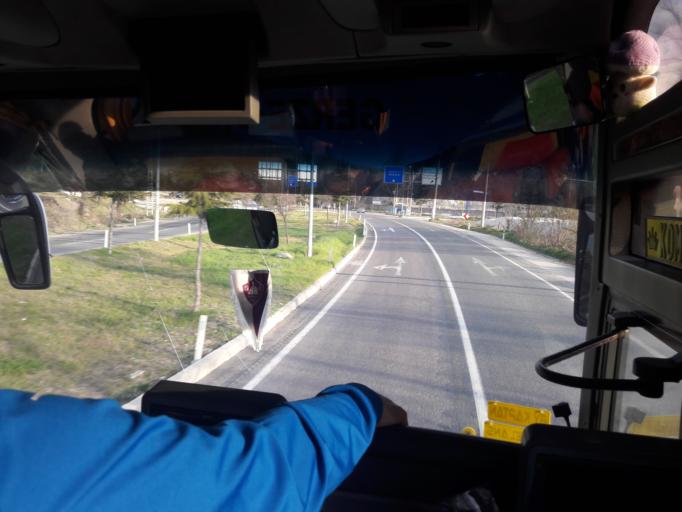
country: TR
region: Cankiri
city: Korgun
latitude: 40.7354
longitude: 33.5197
